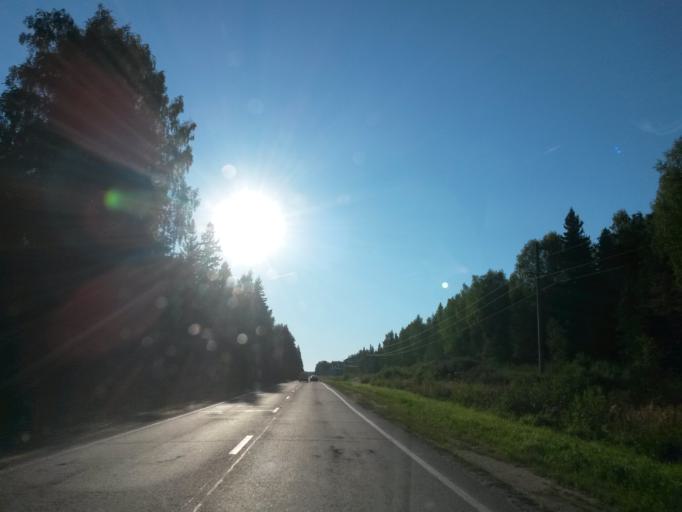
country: RU
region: Jaroslavl
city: Gavrilov-Yam
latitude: 57.2674
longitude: 39.9876
